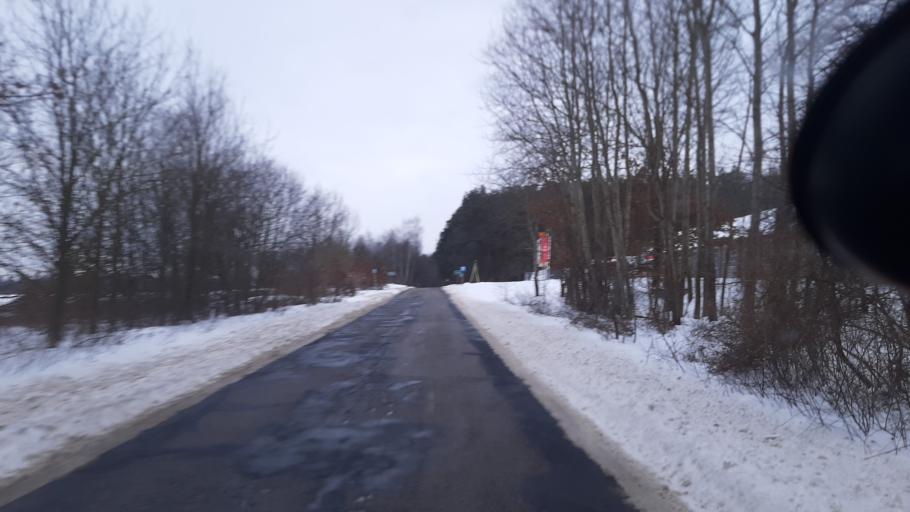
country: PL
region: Lublin Voivodeship
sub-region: Powiat pulawski
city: Kurow
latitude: 51.4311
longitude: 22.2176
